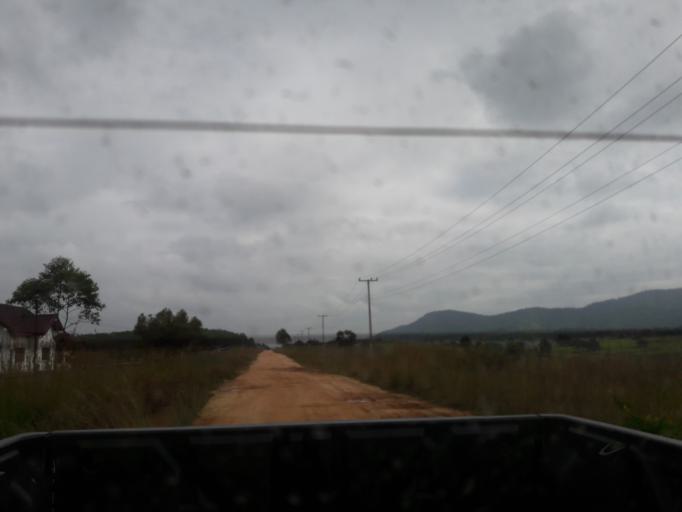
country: LA
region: Xiangkhoang
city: Phonsavan
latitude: 19.5657
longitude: 103.0081
